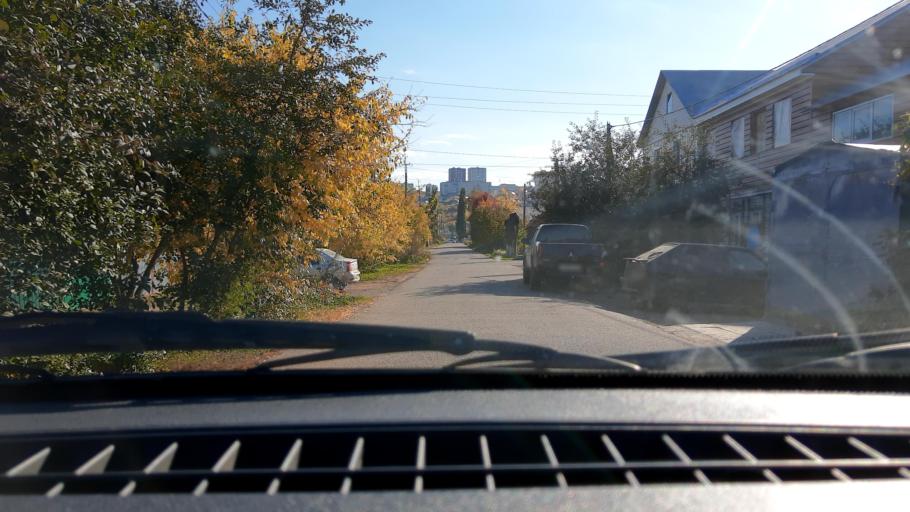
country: RU
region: Bashkortostan
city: Ufa
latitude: 54.7420
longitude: 55.9161
